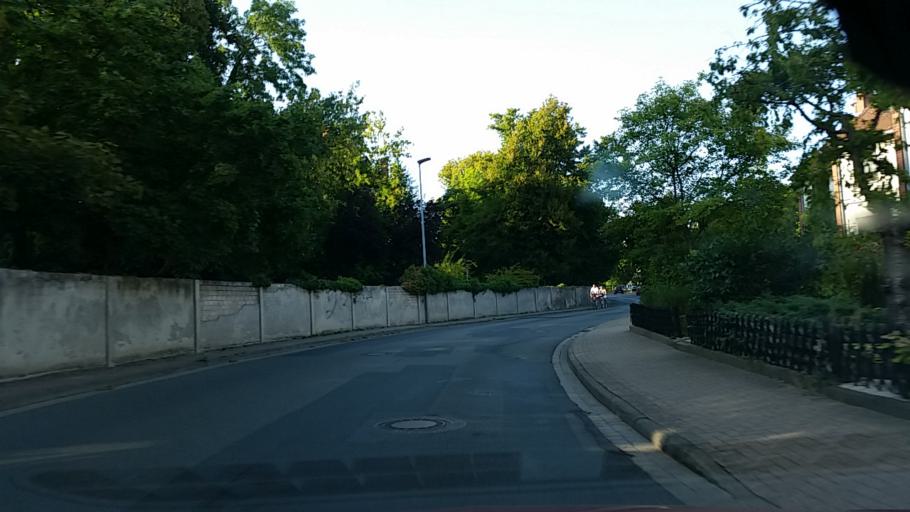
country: DE
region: Lower Saxony
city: Lehre
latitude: 52.3186
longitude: 10.6333
